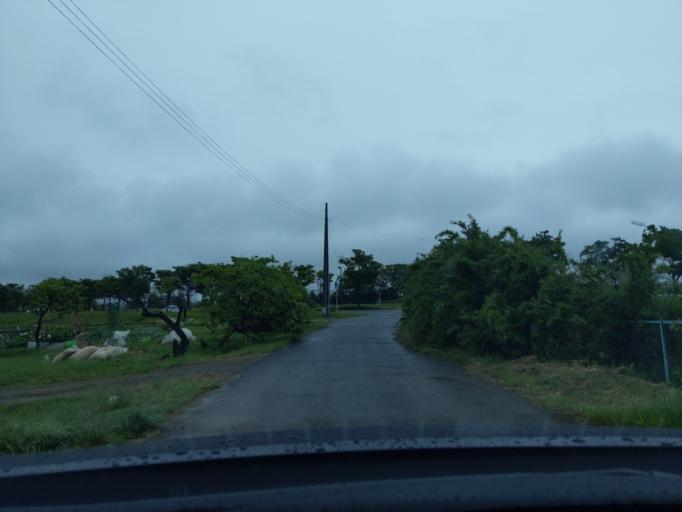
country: JP
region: Fukushima
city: Koriyama
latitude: 37.4486
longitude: 140.3293
